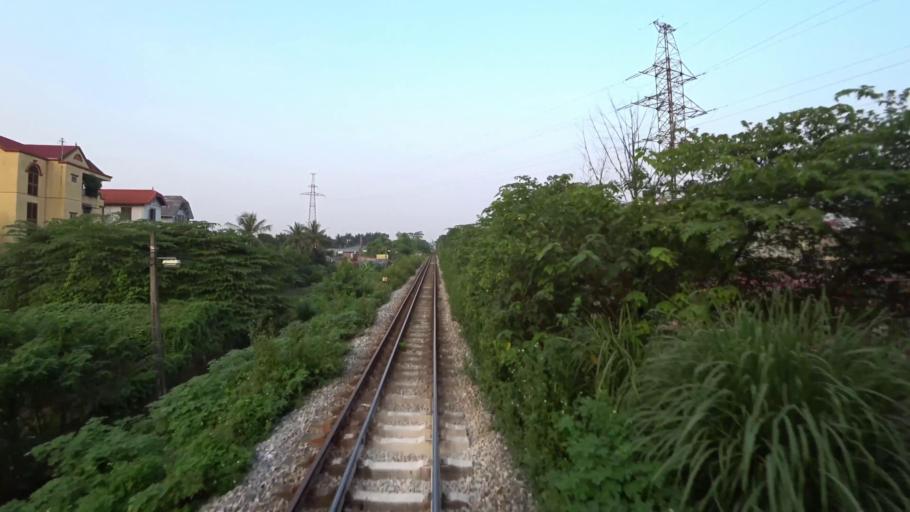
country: VN
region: Ha Noi
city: Trau Quy
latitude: 21.0883
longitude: 105.9188
